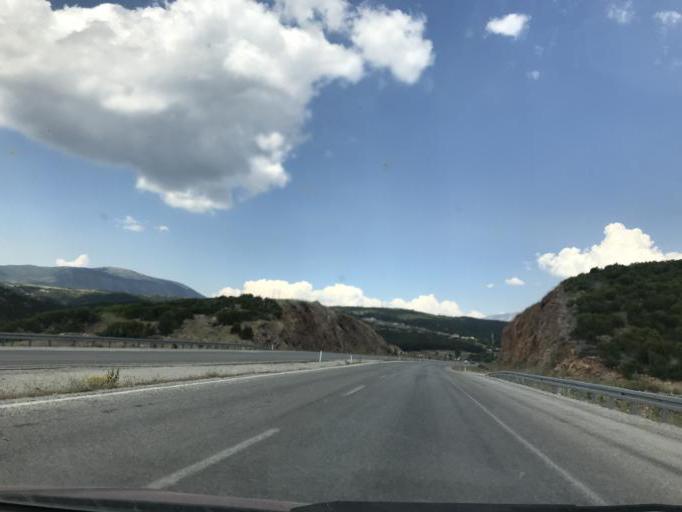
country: TR
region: Denizli
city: Tavas
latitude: 37.6006
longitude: 29.1226
